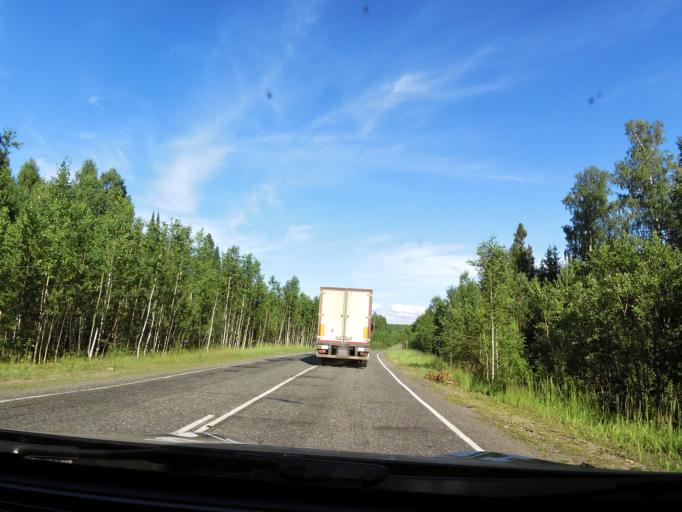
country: RU
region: Kirov
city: Chernaya Kholunitsa
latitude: 58.8762
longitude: 51.4803
